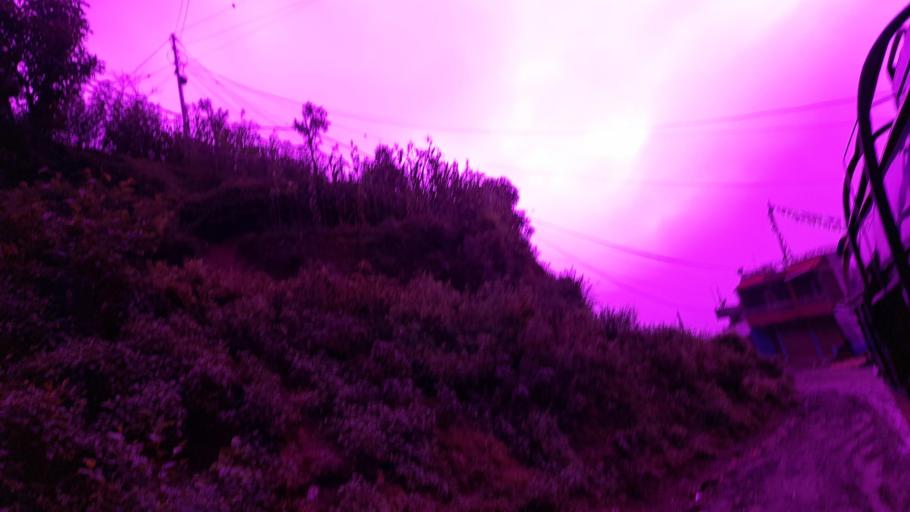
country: NP
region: Central Region
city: Kirtipur
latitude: 27.8177
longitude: 85.2271
